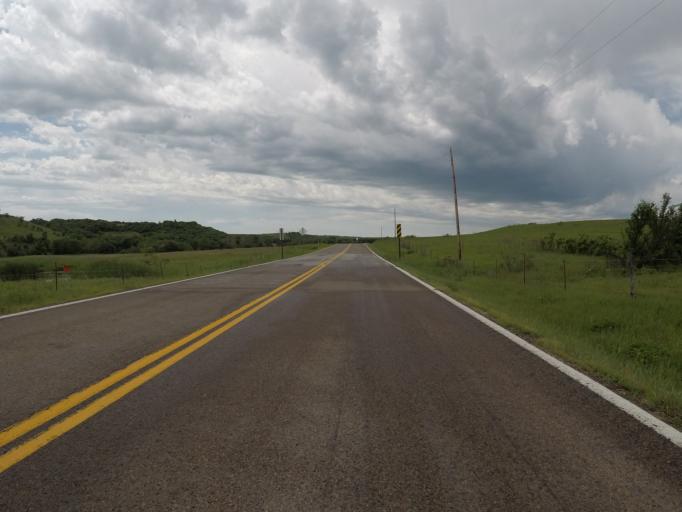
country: US
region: Kansas
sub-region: Wabaunsee County
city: Alma
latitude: 38.8888
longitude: -96.2816
